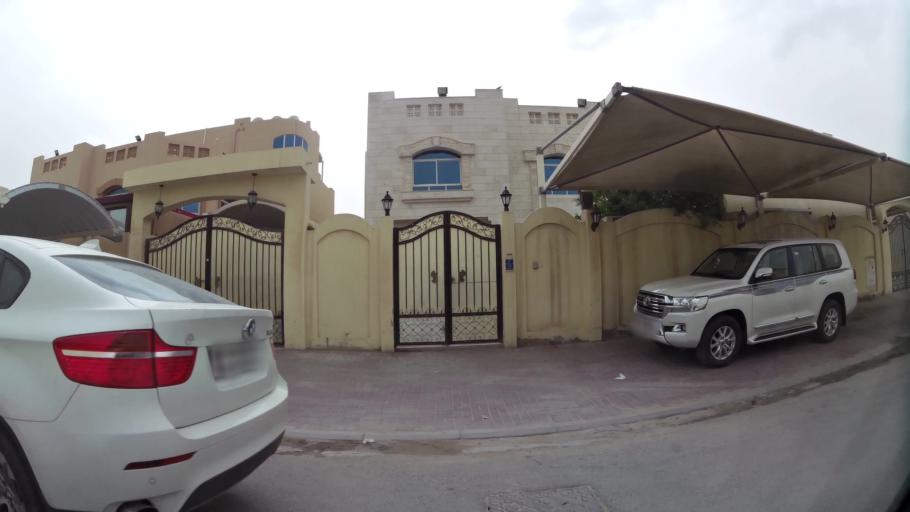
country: QA
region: Baladiyat ad Dawhah
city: Doha
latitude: 25.2457
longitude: 51.5395
